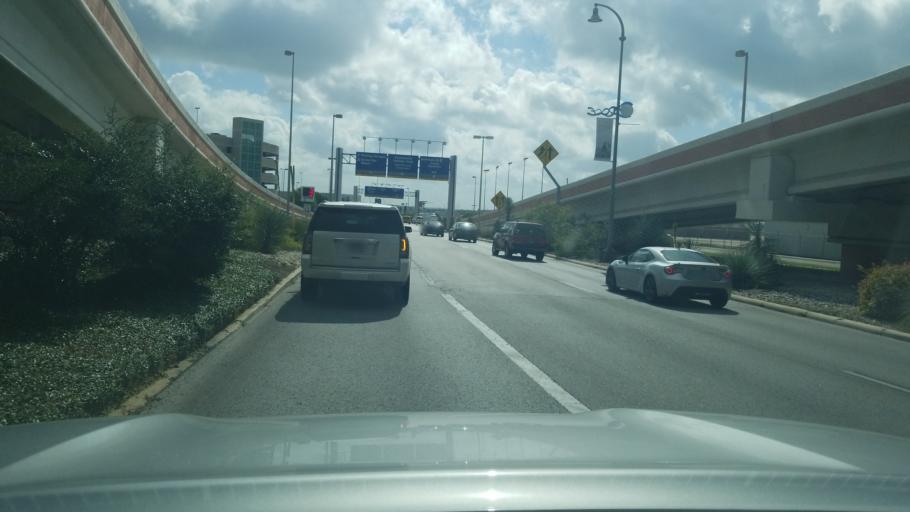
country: US
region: Texas
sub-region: Bexar County
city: Castle Hills
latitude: 29.5245
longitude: -98.4759
